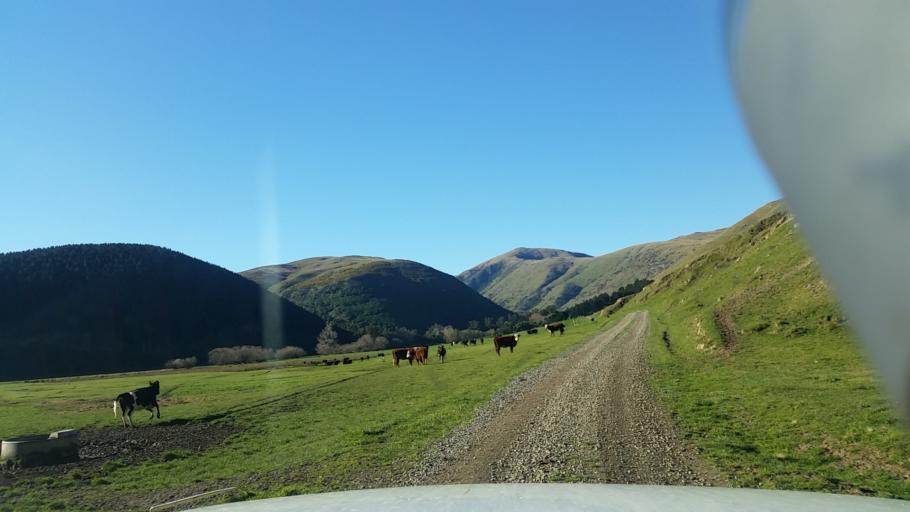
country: NZ
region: Canterbury
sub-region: Selwyn District
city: Lincoln
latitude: -43.7983
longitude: 172.6928
